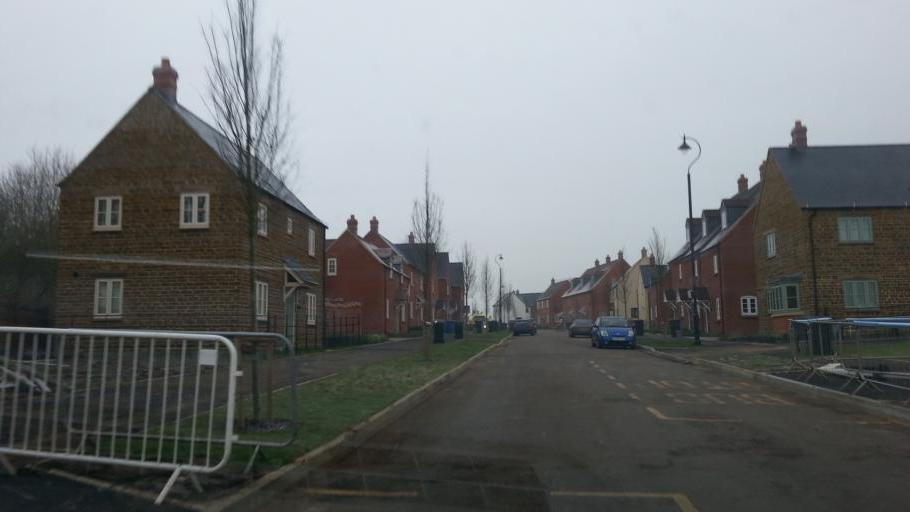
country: GB
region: England
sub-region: Northamptonshire
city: Brackley
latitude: 52.0427
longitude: -1.1417
